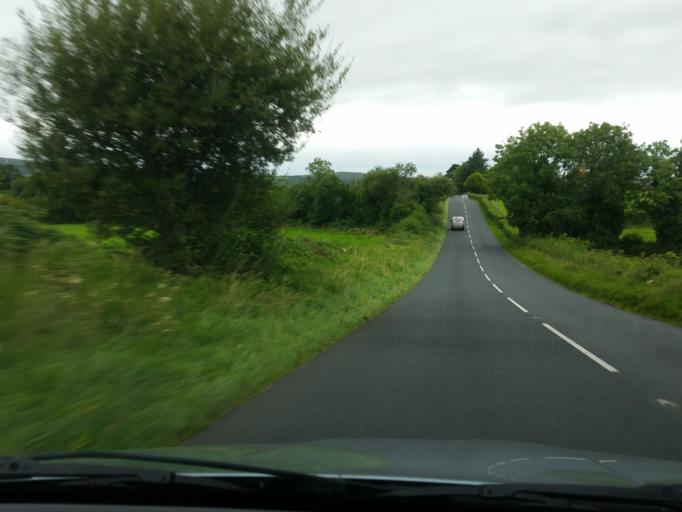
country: IE
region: Ulster
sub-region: An Cabhan
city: Ballyconnell
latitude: 54.1901
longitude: -7.5418
